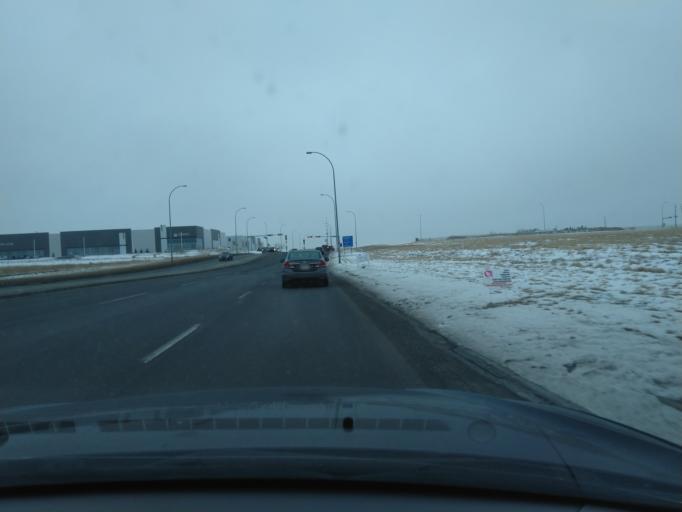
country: CA
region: Alberta
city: Airdrie
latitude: 51.1972
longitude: -113.9910
